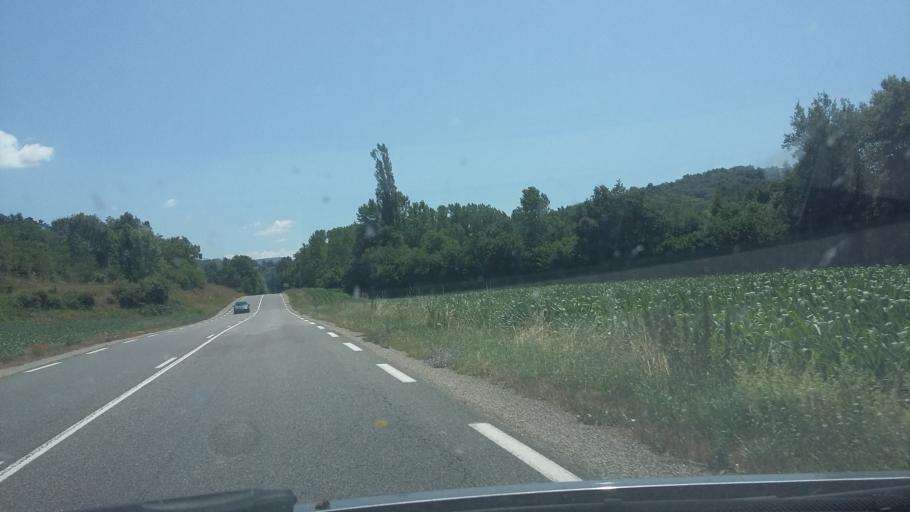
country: FR
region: Rhone-Alpes
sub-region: Departement de l'Ain
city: Belley
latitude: 45.7865
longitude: 5.6853
